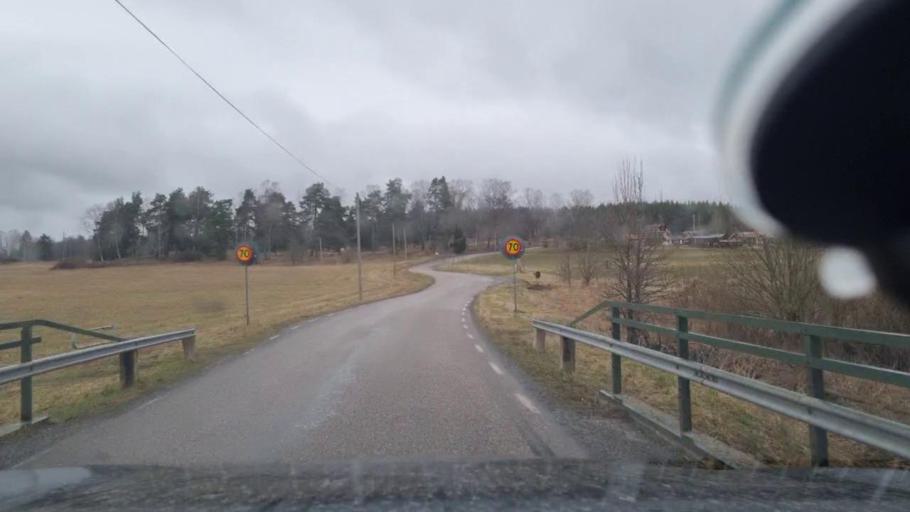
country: SE
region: Stockholm
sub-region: Taby Kommun
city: Taby
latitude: 59.4809
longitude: 18.0147
